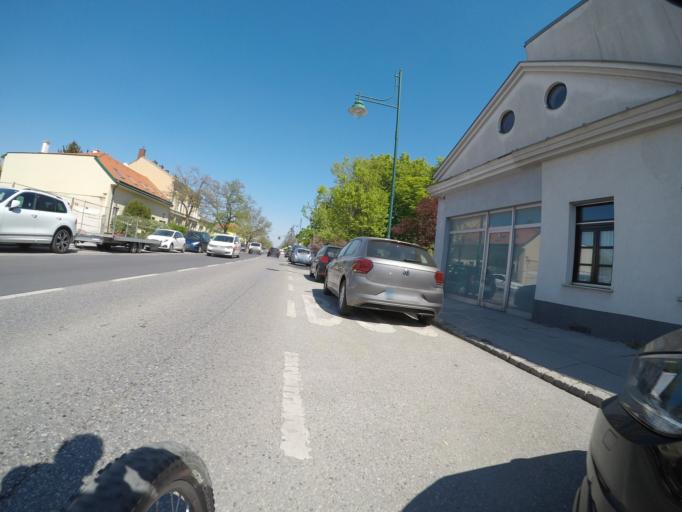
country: AT
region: Lower Austria
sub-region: Politischer Bezirk Modling
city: Wiener Neudorf
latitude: 48.0872
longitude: 16.3021
